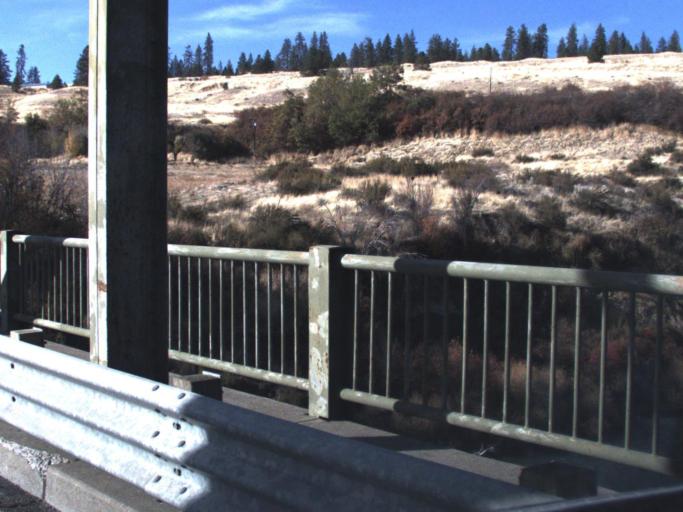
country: US
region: Washington
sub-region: Lincoln County
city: Davenport
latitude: 47.9080
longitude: -118.3188
